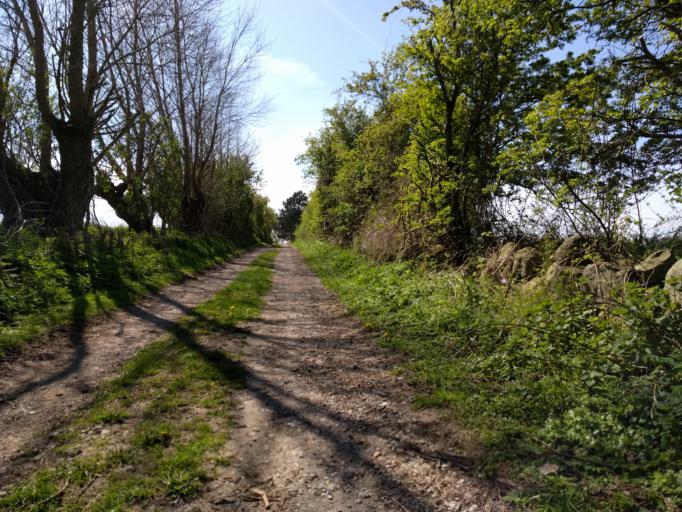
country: DK
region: South Denmark
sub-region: Kerteminde Kommune
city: Munkebo
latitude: 55.4534
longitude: 10.5907
